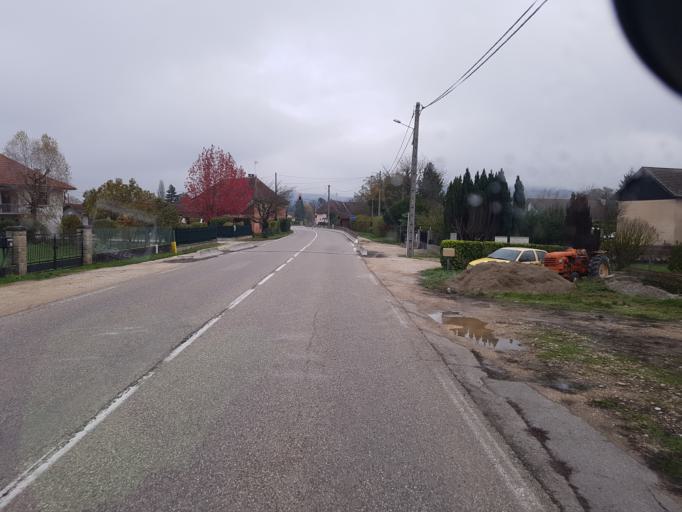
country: FR
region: Rhone-Alpes
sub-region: Departement de l'Isere
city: Aoste
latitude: 45.5936
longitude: 5.6201
